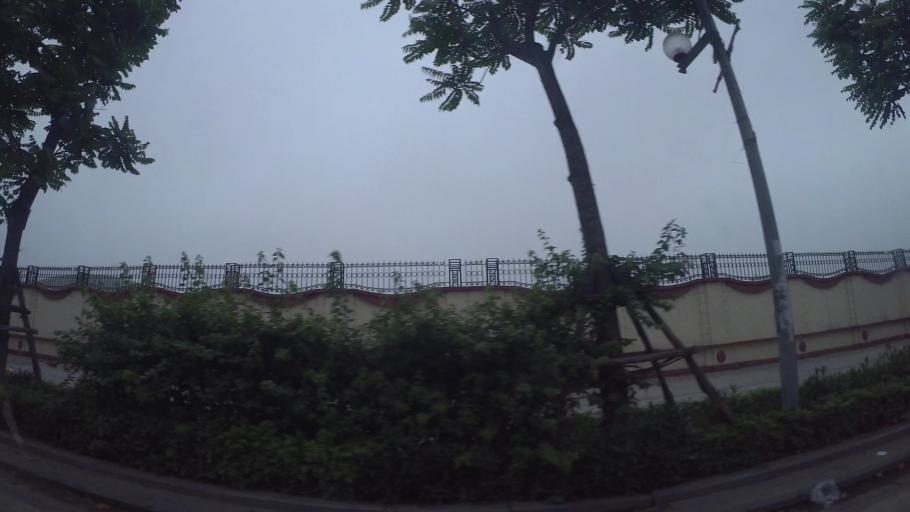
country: VN
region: Ha Noi
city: Dong Da
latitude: 20.9967
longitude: 105.8309
